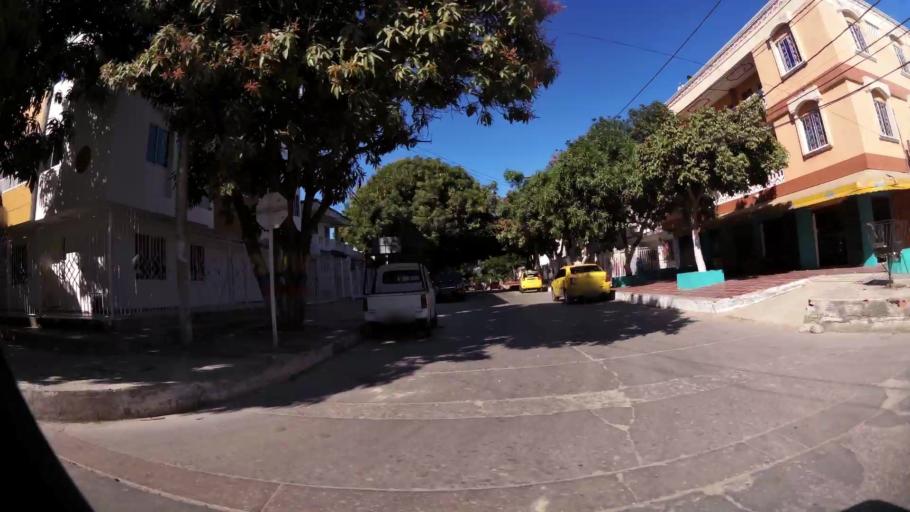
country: CO
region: Atlantico
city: Barranquilla
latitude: 10.9584
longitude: -74.7903
